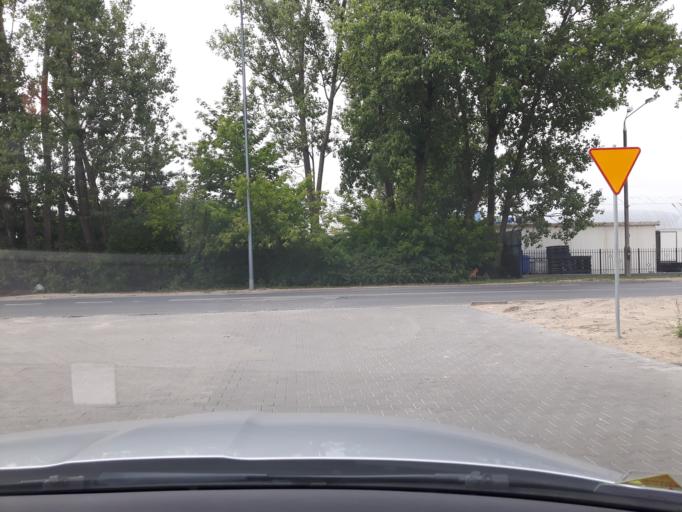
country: PL
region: Masovian Voivodeship
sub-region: Powiat wolominski
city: Zabki
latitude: 52.2754
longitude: 21.1169
